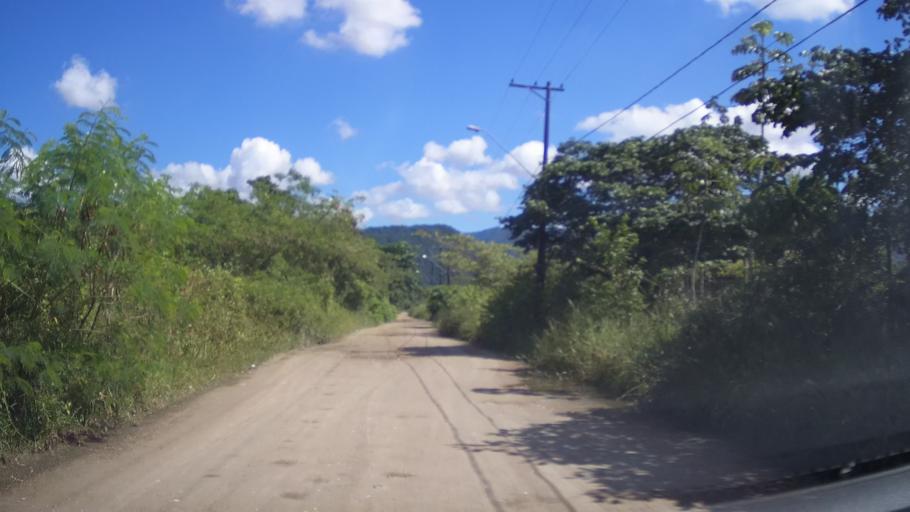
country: BR
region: Sao Paulo
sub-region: Praia Grande
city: Praia Grande
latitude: -24.0136
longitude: -46.5107
